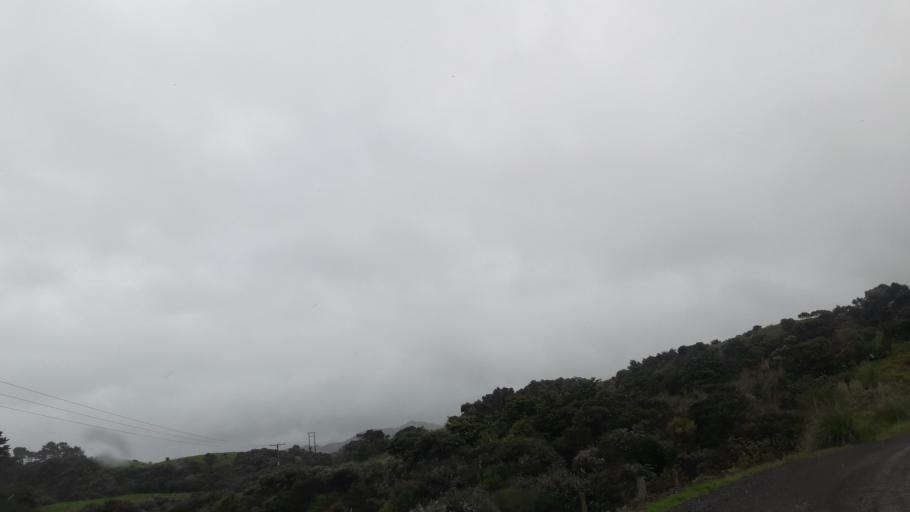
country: NZ
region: Northland
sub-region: Far North District
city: Kaitaia
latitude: -35.4106
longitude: 173.3652
